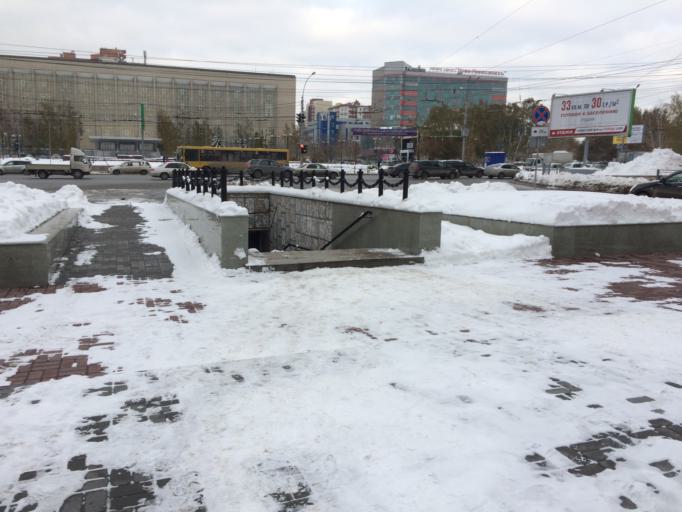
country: RU
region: Novosibirsk
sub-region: Novosibirskiy Rayon
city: Novosibirsk
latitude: 55.0157
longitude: 82.9452
